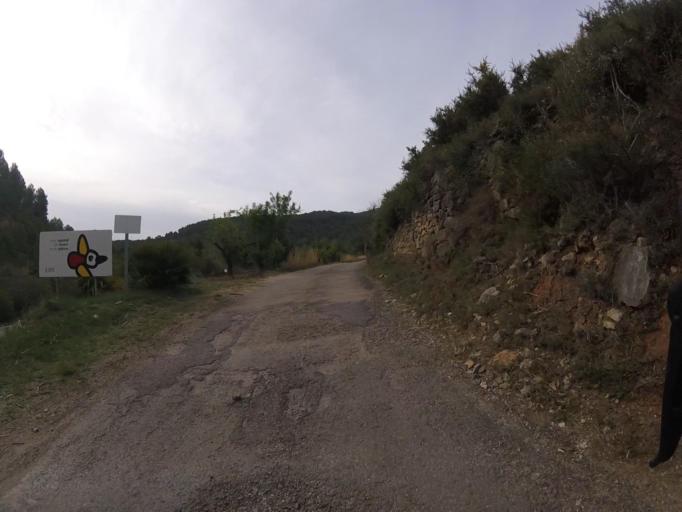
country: ES
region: Valencia
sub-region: Provincia de Castello
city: Cabanes
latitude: 40.1165
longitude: 0.0477
